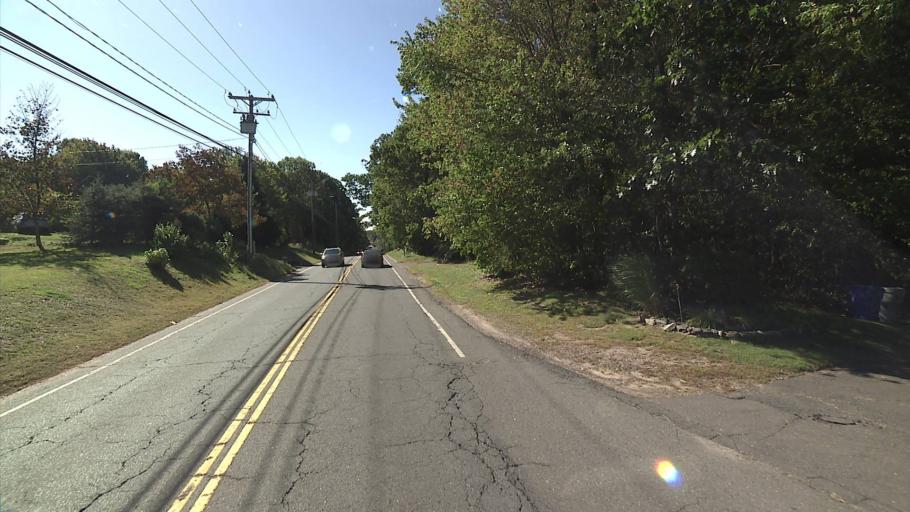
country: US
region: Connecticut
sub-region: Hartford County
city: Bristol
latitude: 41.6421
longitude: -72.9639
